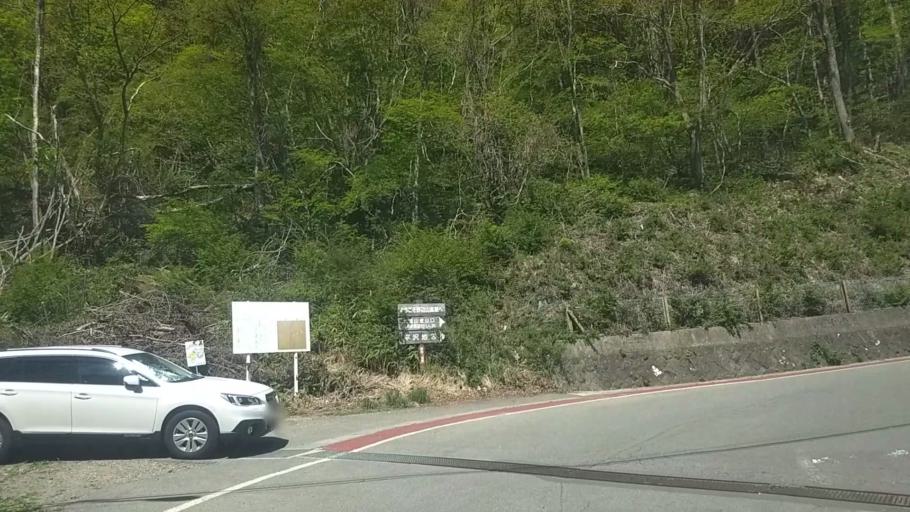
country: JP
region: Yamanashi
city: Nirasaki
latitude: 35.9216
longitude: 138.4445
